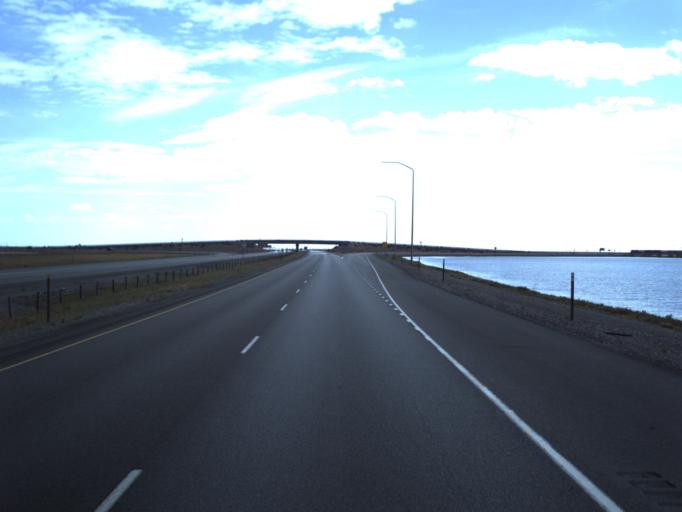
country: US
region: Utah
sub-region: Tooele County
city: Wendover
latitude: 40.7430
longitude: -113.9785
